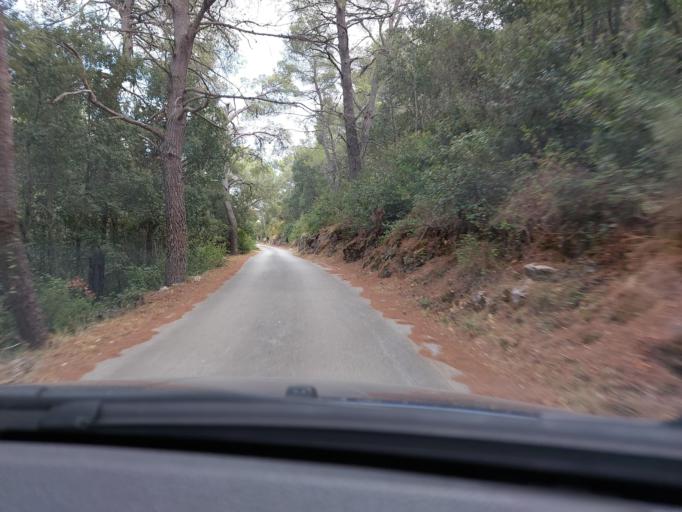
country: HR
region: Dubrovacko-Neretvanska
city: Smokvica
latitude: 42.7635
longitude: 16.9080
